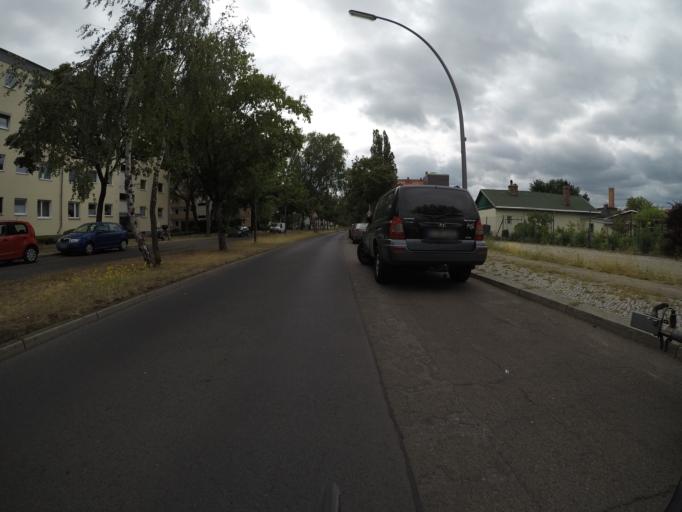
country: DE
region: Berlin
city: Reinickendorf
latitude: 52.5612
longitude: 13.3410
